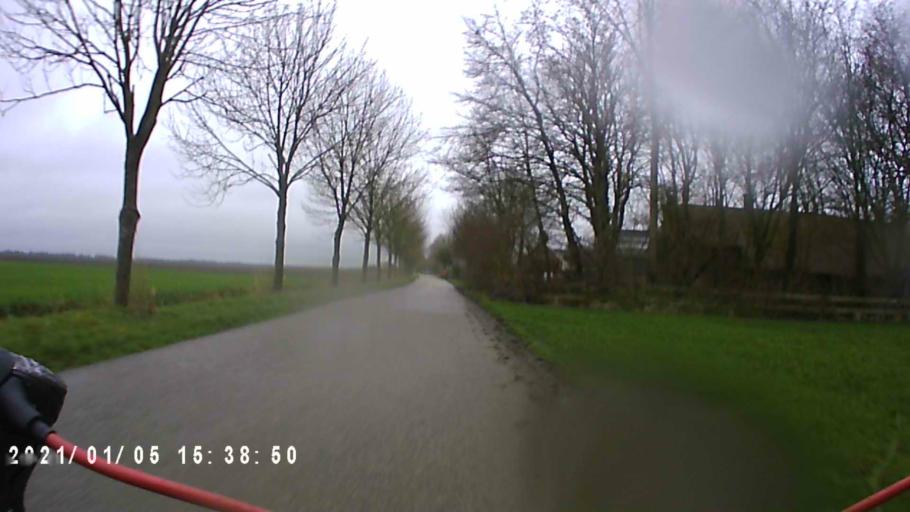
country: DE
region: Lower Saxony
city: Bunde
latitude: 53.2122
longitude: 7.1534
